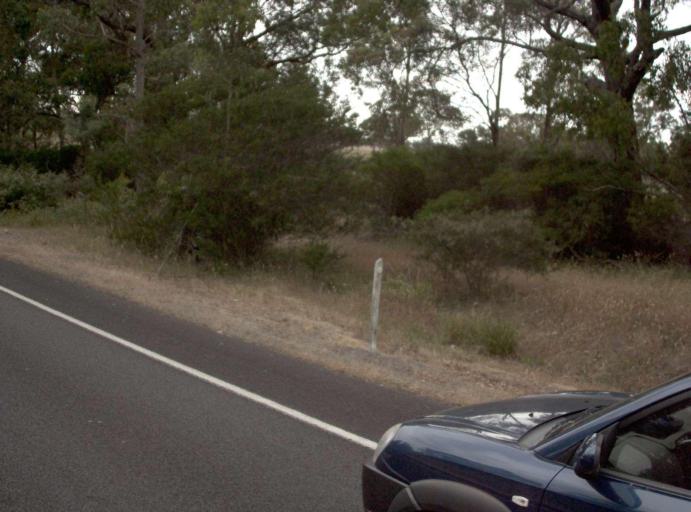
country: AU
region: Victoria
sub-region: Wellington
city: Sale
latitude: -38.4471
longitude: 146.9427
